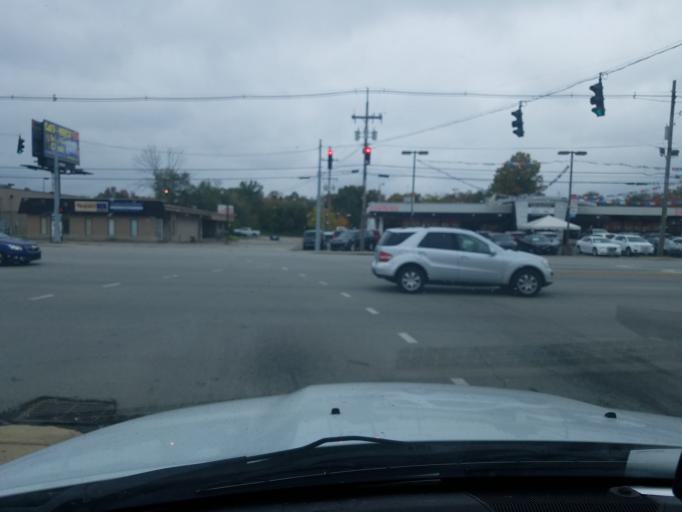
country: US
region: Kentucky
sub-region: Jefferson County
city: Pleasure Ridge Park
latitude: 38.1521
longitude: -85.8360
